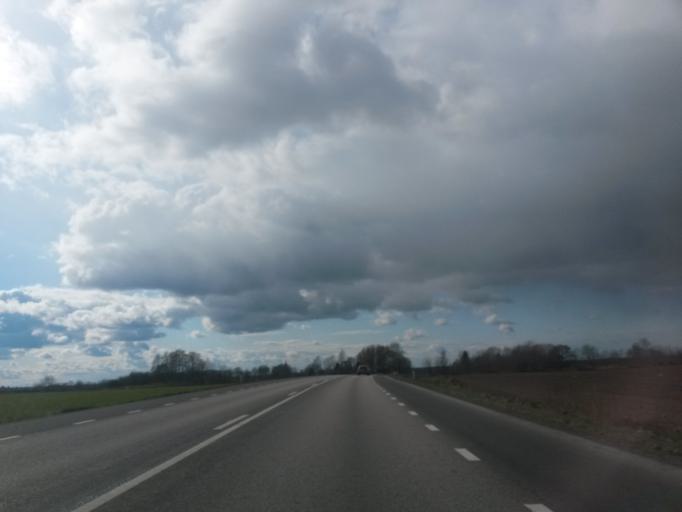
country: SE
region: Vaestra Goetaland
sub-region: Skara Kommun
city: Axvall
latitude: 58.3834
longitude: 13.6702
